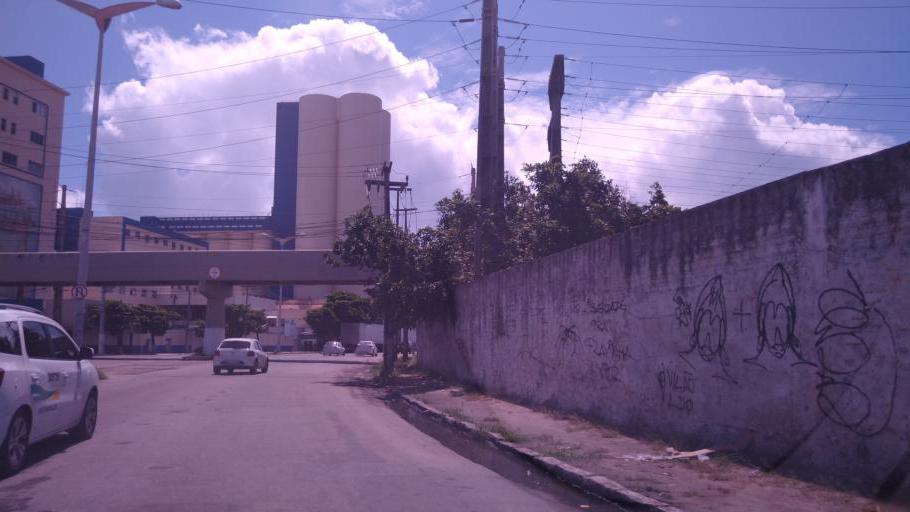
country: BR
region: Ceara
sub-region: Fortaleza
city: Fortaleza
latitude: -3.7171
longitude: -38.4752
